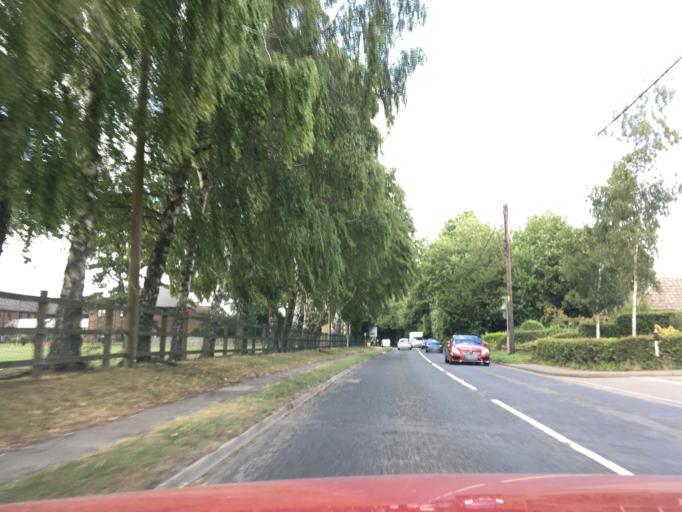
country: GB
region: England
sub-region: Kent
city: Headcorn
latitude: 51.2194
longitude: 0.5932
